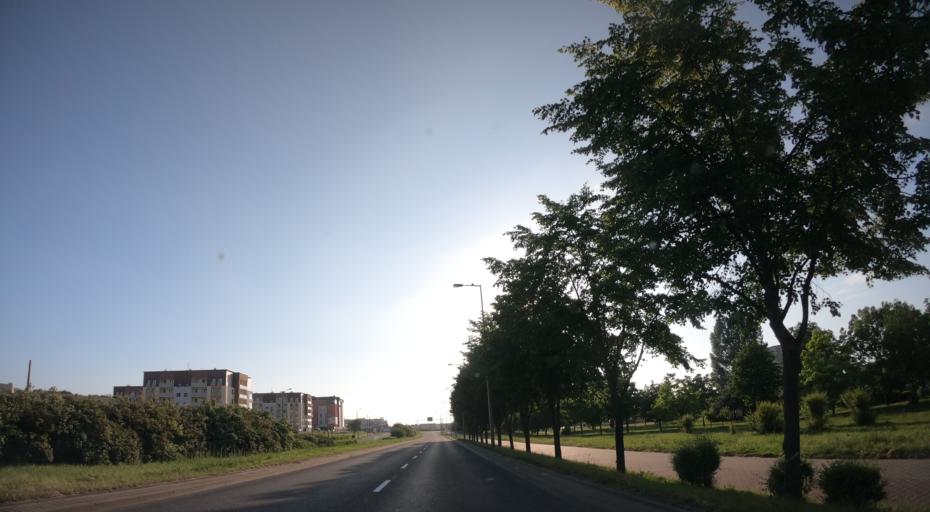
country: PL
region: Lubusz
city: Gorzow Wielkopolski
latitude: 52.7584
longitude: 15.2620
